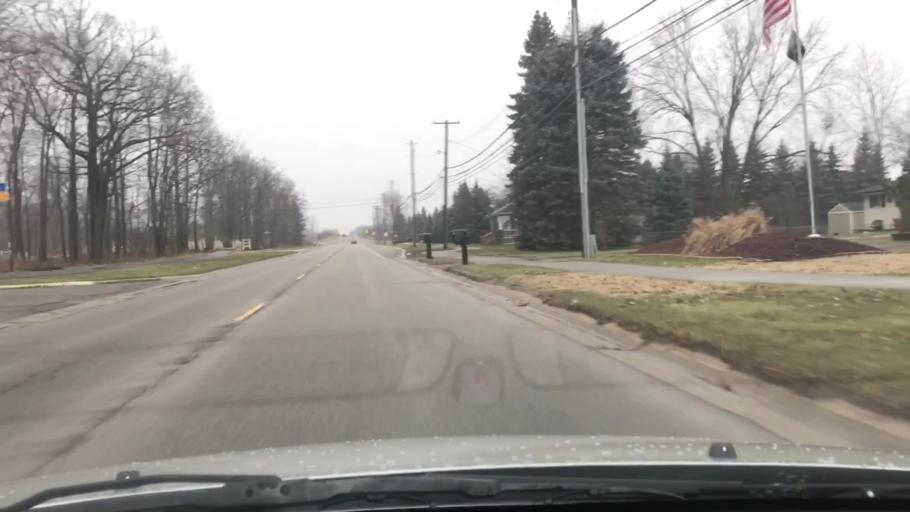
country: US
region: Michigan
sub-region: Oakland County
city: Rochester Hills
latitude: 42.6465
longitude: -83.1526
